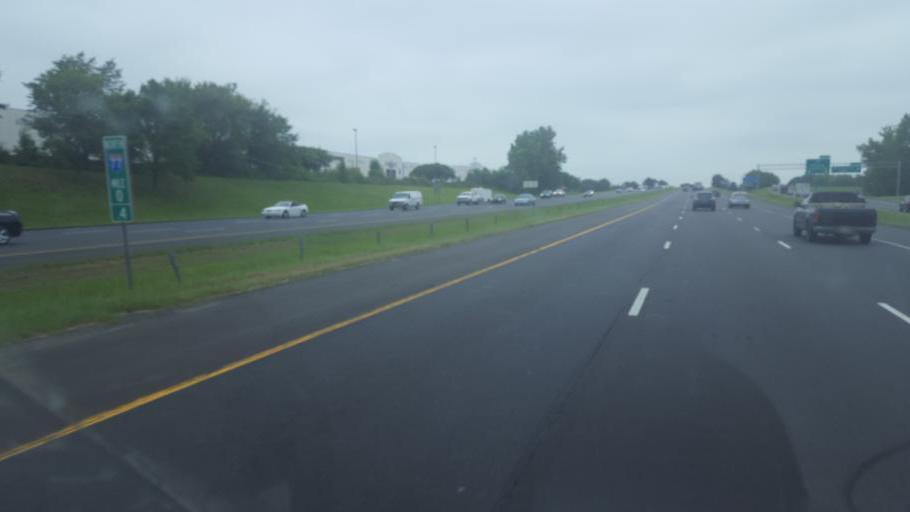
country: US
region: North Carolina
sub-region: Mecklenburg County
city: Pineville
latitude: 35.1091
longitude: -80.9279
